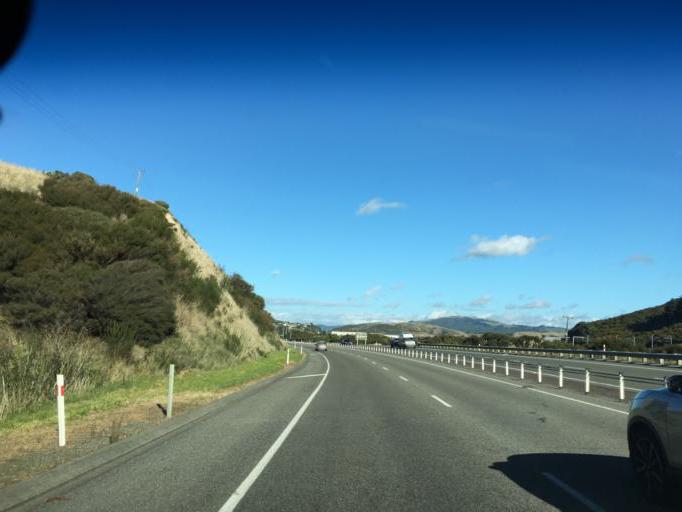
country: NZ
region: Wellington
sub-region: Porirua City
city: Porirua
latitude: -41.0708
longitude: 174.8763
